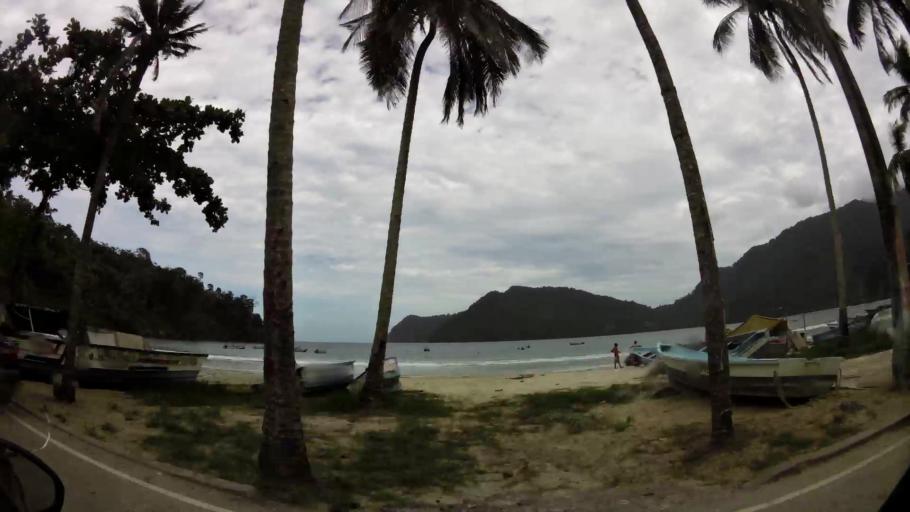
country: TT
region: Diego Martin
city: Petit Valley
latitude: 10.7623
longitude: -61.4436
